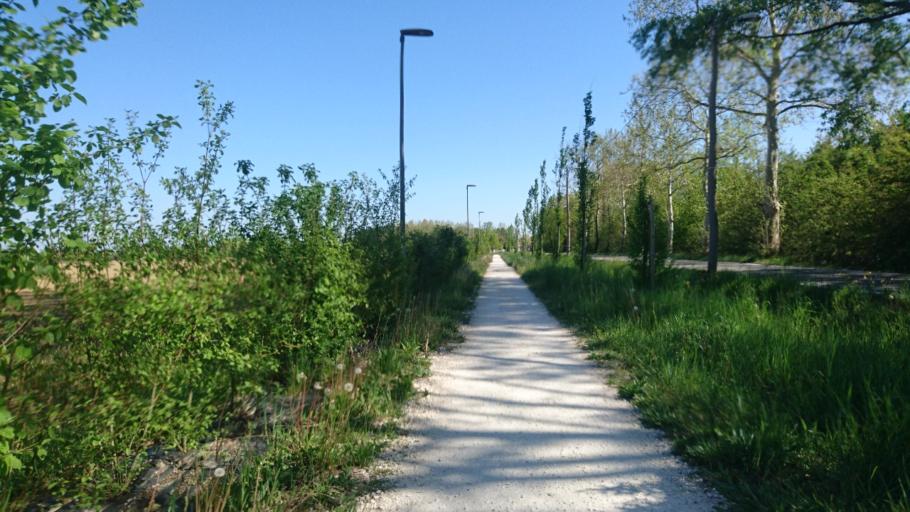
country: IT
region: Veneto
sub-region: Provincia di Treviso
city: Mogliano Veneto
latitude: 45.5161
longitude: 12.2582
